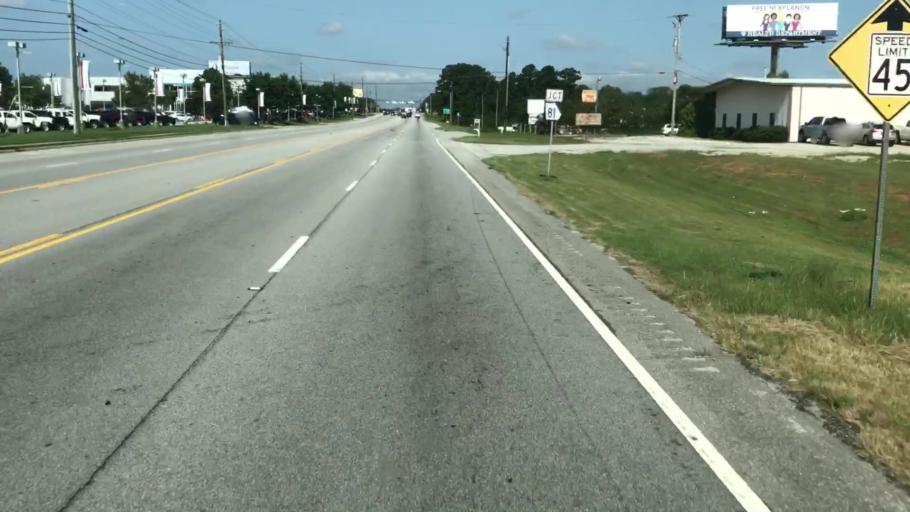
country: US
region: Georgia
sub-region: Walton County
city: Loganville
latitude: 33.8320
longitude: -83.8767
